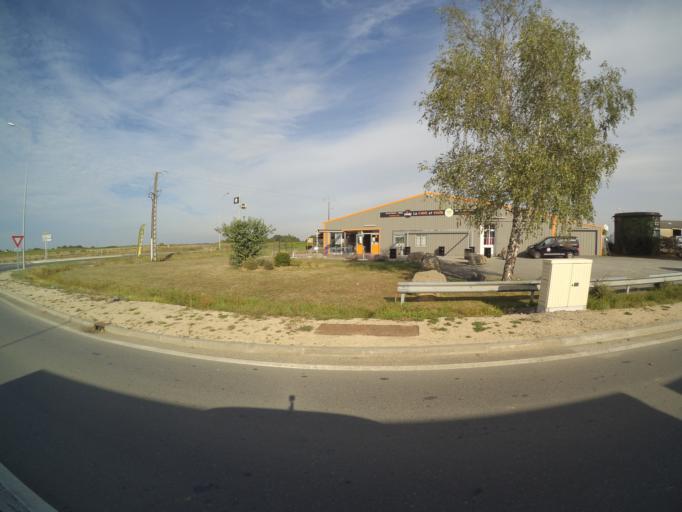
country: FR
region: Pays de la Loire
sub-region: Departement de la Loire-Atlantique
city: Mouzillon
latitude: 47.1257
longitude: -1.2821
